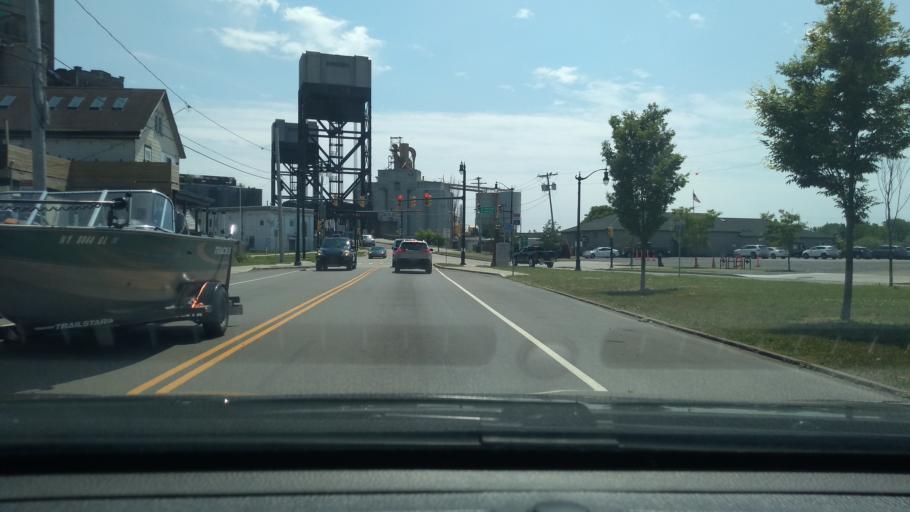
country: US
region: New York
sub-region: Erie County
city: Buffalo
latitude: 42.8638
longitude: -78.8671
